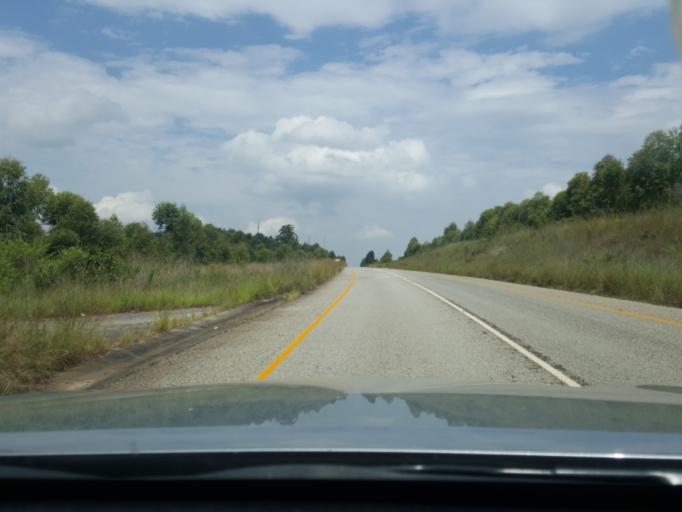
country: ZA
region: Mpumalanga
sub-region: Ehlanzeni District
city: White River
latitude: -25.1906
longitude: 30.9063
